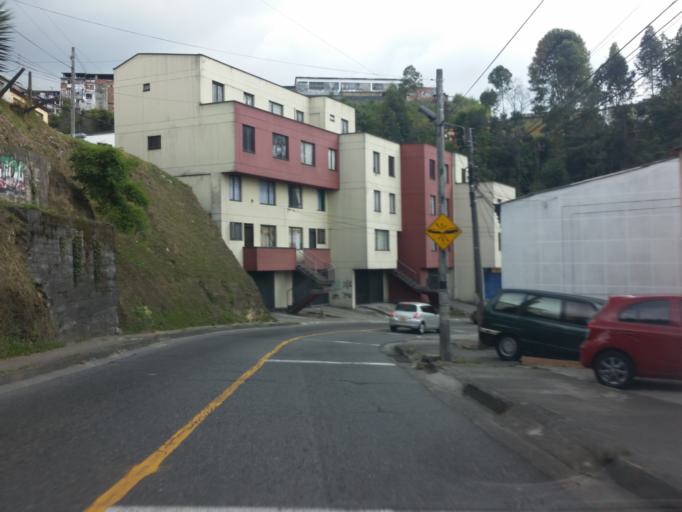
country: CO
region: Caldas
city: Manizales
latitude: 5.0623
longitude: -75.5057
